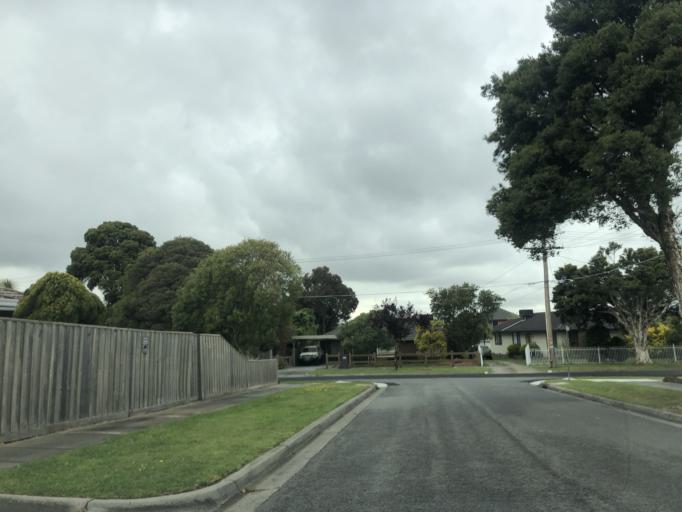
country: AU
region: Victoria
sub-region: Greater Dandenong
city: Dandenong North
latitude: -37.9589
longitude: 145.2140
